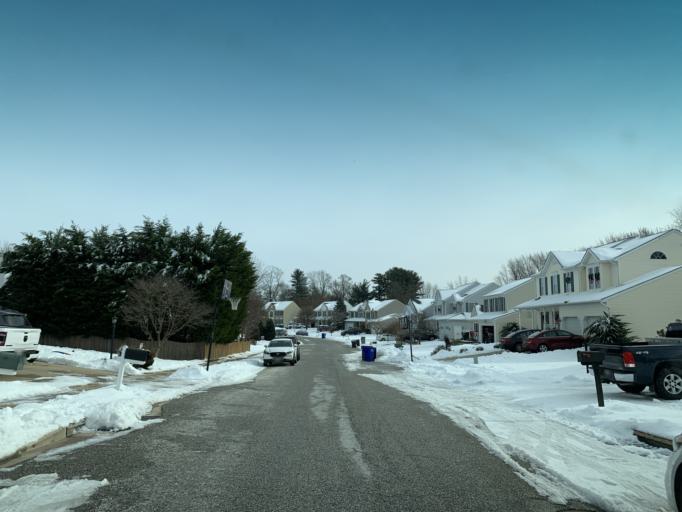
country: US
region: Maryland
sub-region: Harford County
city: Bel Air North
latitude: 39.5763
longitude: -76.3561
